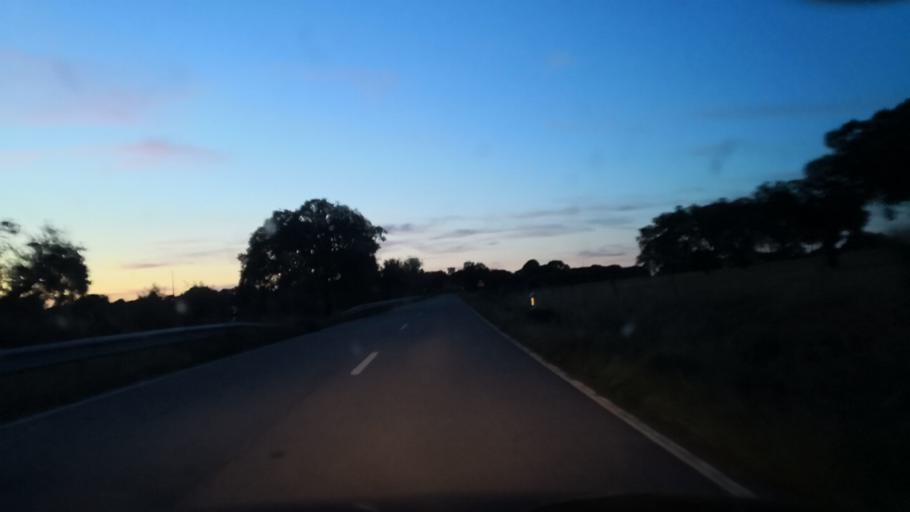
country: ES
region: Extremadura
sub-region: Provincia de Caceres
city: Piedras Albas
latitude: 39.8458
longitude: -6.9805
